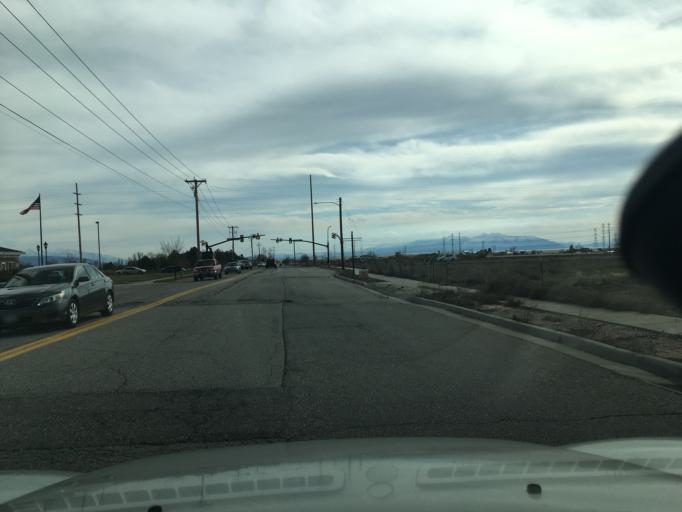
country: US
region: Utah
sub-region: Davis County
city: Layton
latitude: 41.0688
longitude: -112.0071
